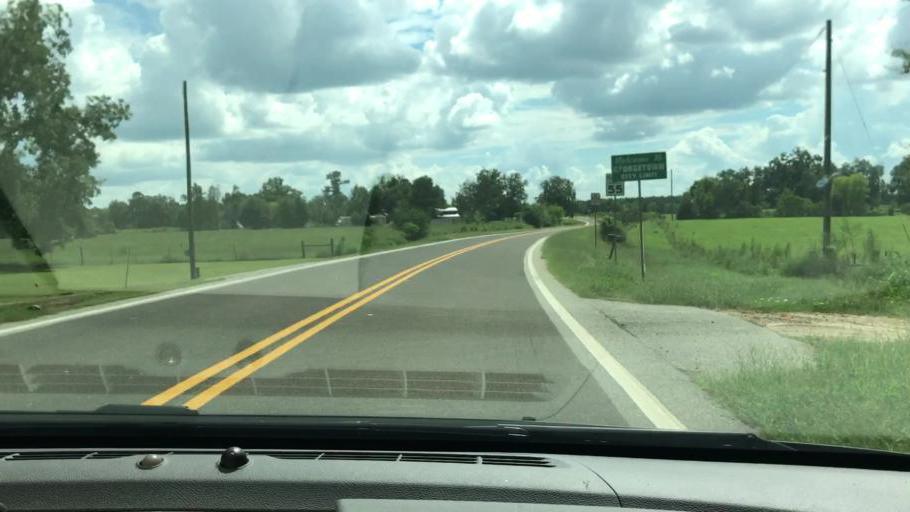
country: US
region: Georgia
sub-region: Quitman County
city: Georgetown
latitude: 31.8958
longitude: -85.0811
